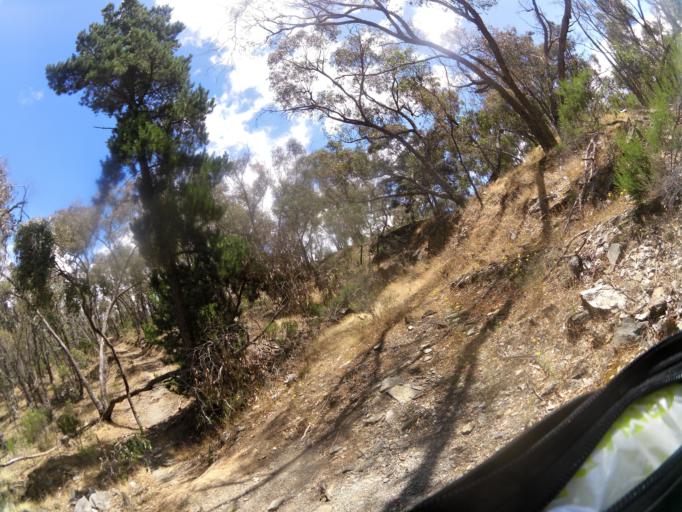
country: AU
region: Victoria
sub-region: Mount Alexander
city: Castlemaine
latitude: -37.0618
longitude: 144.2672
